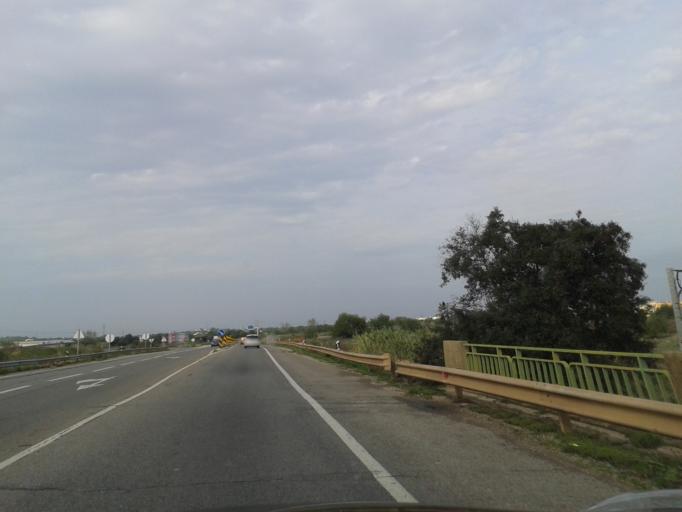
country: PT
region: Faro
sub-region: Albufeira
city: Ferreiras
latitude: 37.1241
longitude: -8.2528
